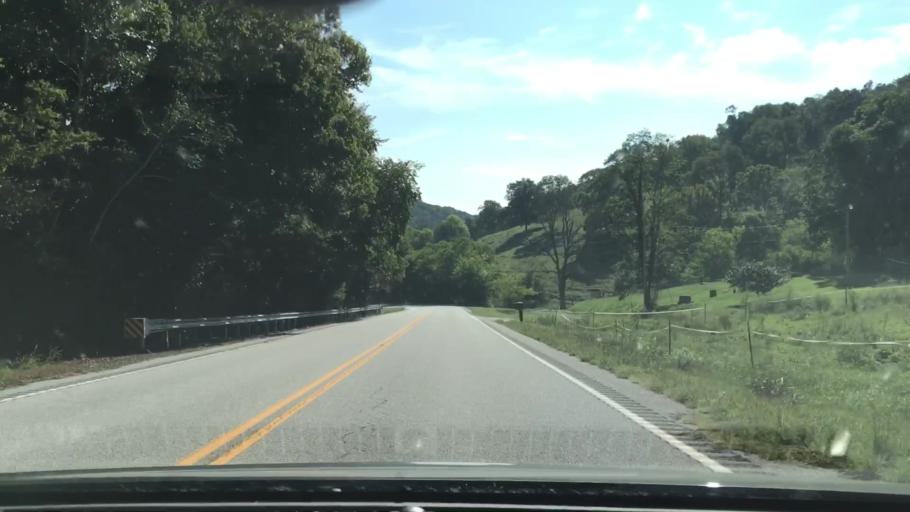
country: US
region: Tennessee
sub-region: Jackson County
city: Gainesboro
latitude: 36.3645
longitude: -85.7643
